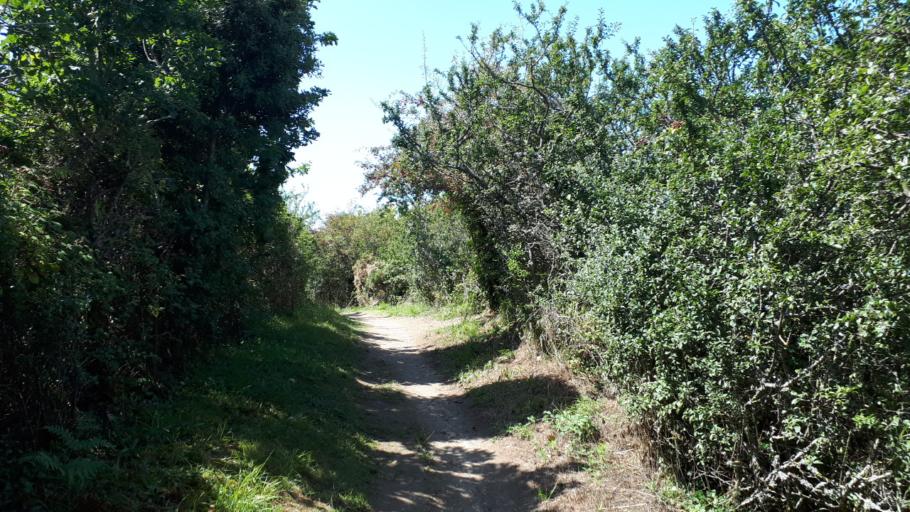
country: FR
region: Brittany
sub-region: Departement du Morbihan
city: Penestin
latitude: 47.4948
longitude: -2.4857
